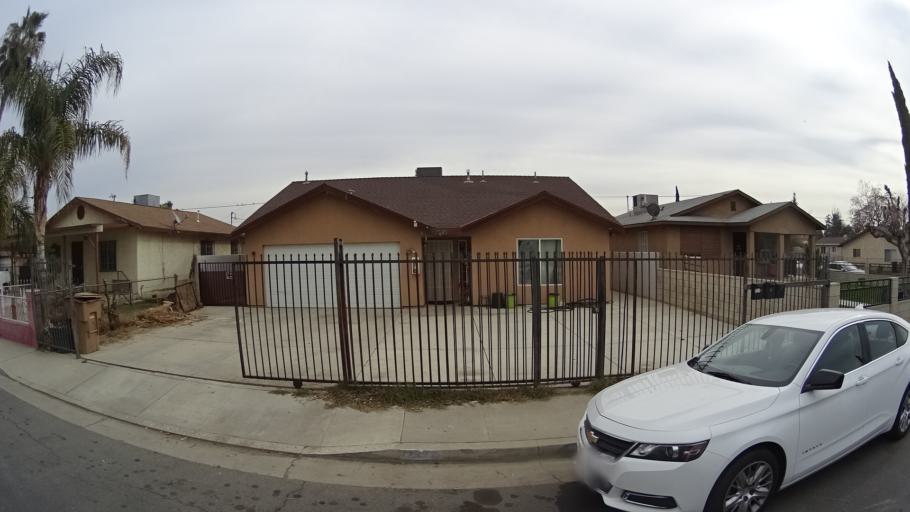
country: US
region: California
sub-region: Kern County
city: Bakersfield
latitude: 35.3638
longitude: -118.9827
